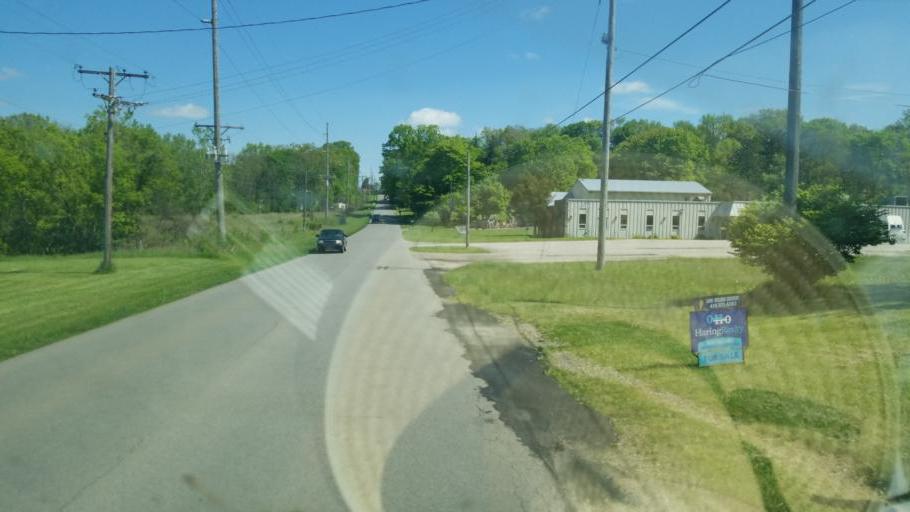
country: US
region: Ohio
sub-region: Richland County
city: Lincoln Heights
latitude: 40.7638
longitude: -82.4842
